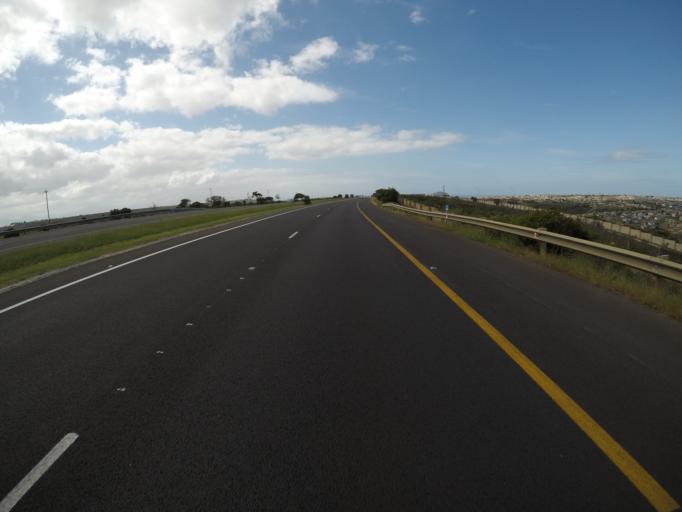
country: ZA
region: Western Cape
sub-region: Eden District Municipality
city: Mossel Bay
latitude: -34.1734
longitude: 22.0691
